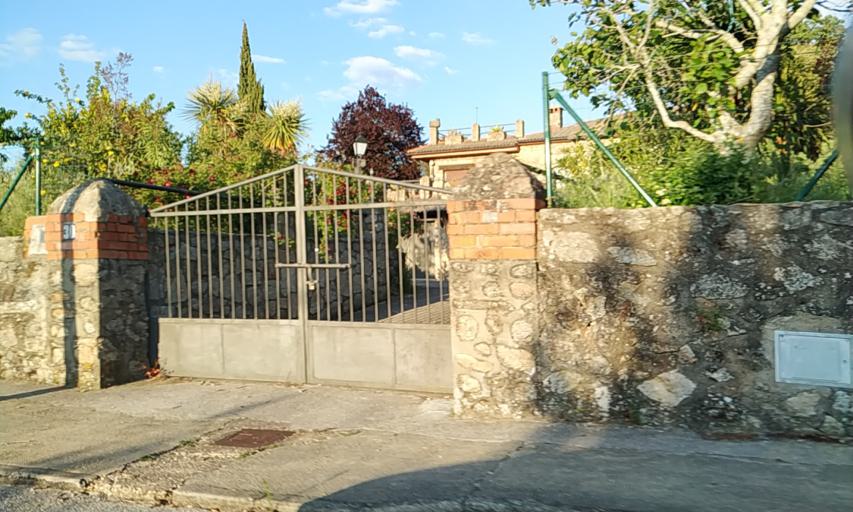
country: PT
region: Portalegre
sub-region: Portalegre
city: Sao Juliao
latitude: 39.3499
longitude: -7.2748
